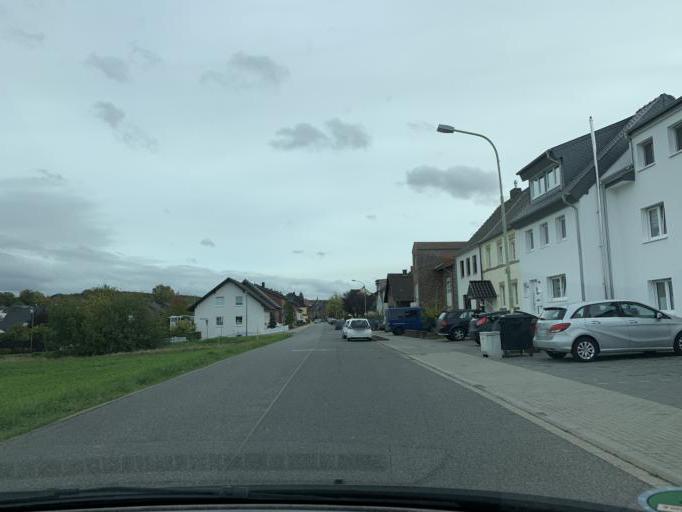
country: DE
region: North Rhine-Westphalia
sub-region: Regierungsbezirk Koln
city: Kreuzau
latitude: 50.7358
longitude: 6.5069
